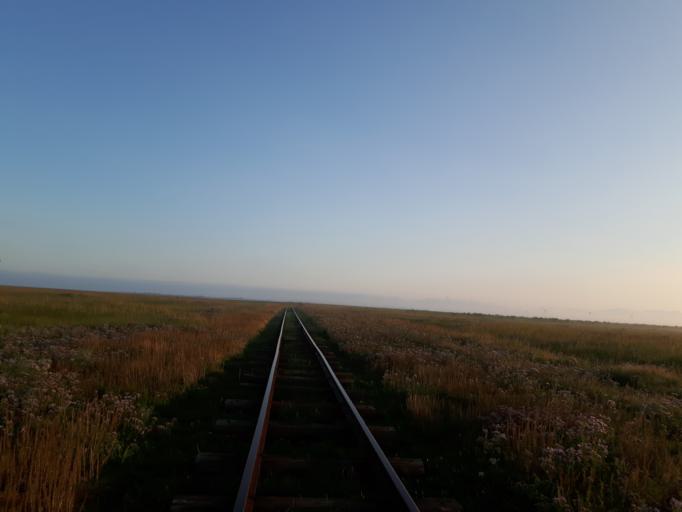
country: DE
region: Schleswig-Holstein
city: Dagebull
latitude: 54.6828
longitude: 8.7099
